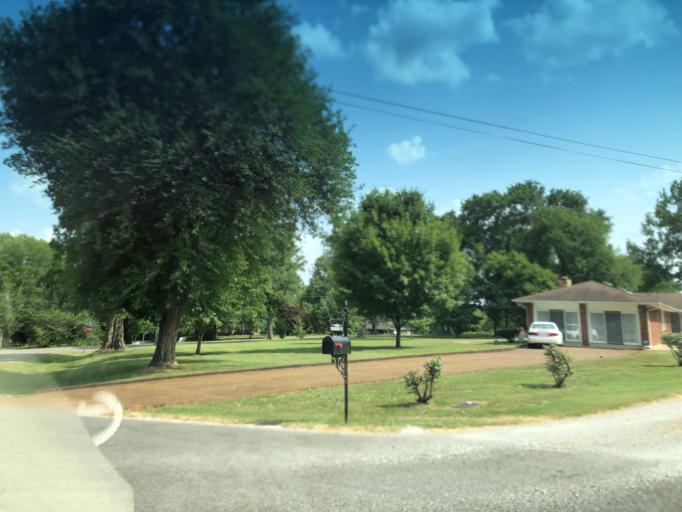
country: US
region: Tennessee
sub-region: Davidson County
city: Goodlettsville
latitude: 36.2536
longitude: -86.7320
